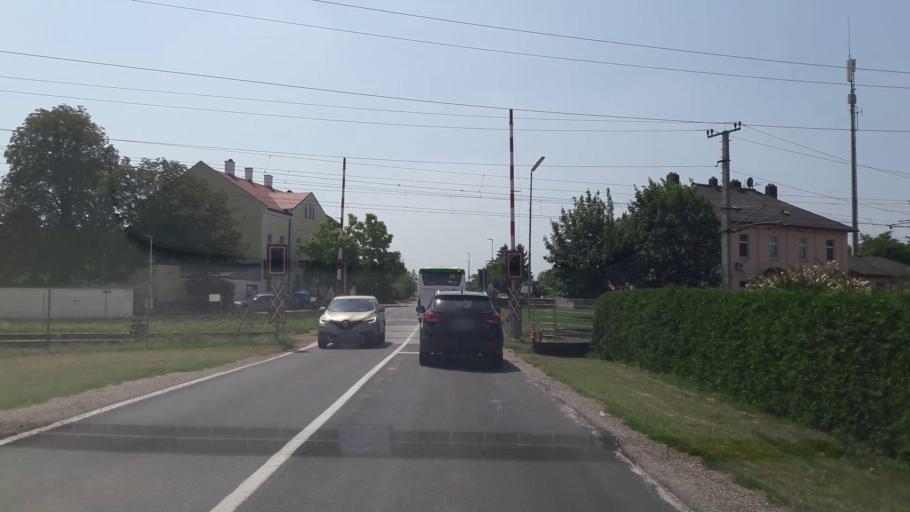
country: AT
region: Lower Austria
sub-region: Politischer Bezirk Bruck an der Leitha
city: Gotzendorf an der Leitha
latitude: 48.0259
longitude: 16.5894
